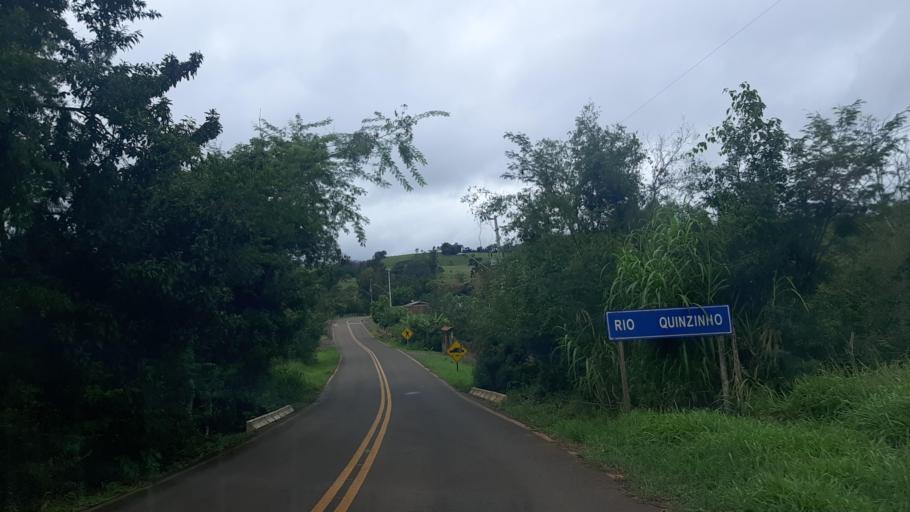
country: BR
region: Parana
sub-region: Ampere
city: Ampere
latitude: -25.9750
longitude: -53.4440
